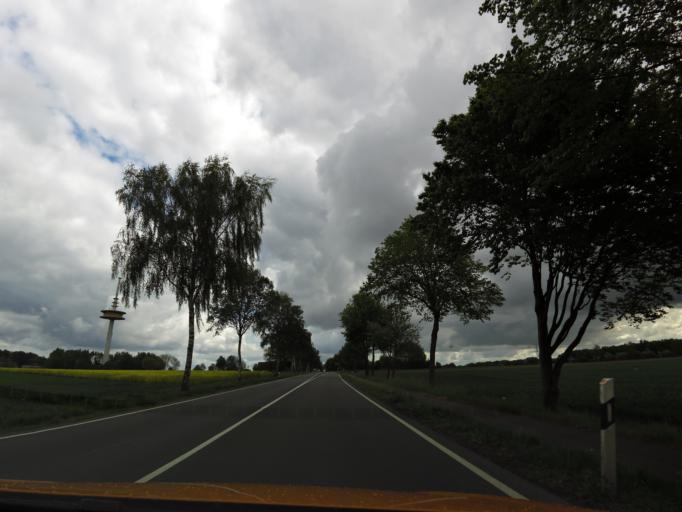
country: DE
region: Lower Saxony
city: Bassum
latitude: 52.8277
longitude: 8.6915
